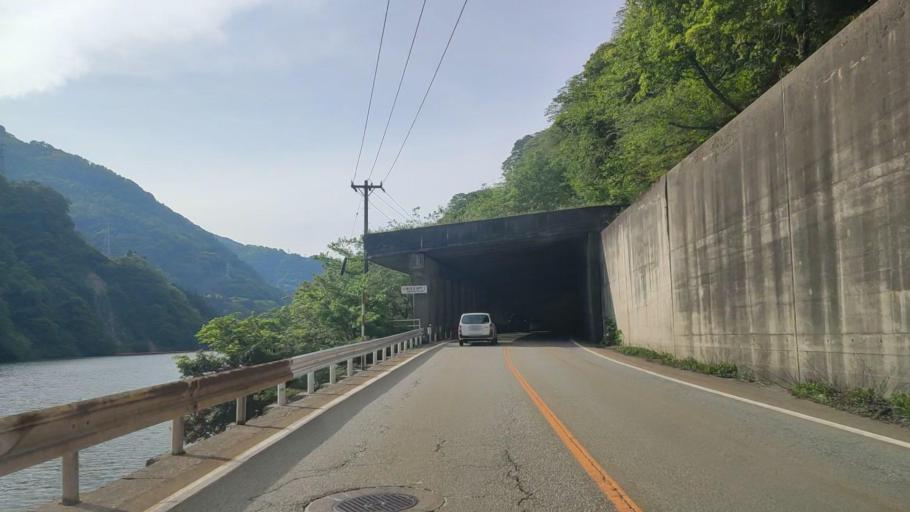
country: JP
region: Toyama
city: Yatsuomachi-higashikumisaka
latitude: 36.4243
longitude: 137.2841
